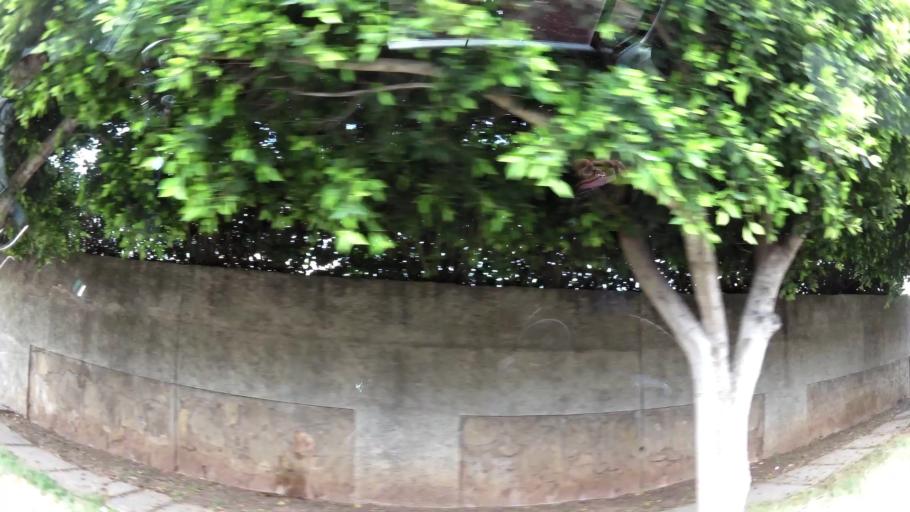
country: MA
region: Rabat-Sale-Zemmour-Zaer
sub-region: Rabat
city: Rabat
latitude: 33.9867
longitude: -6.8333
